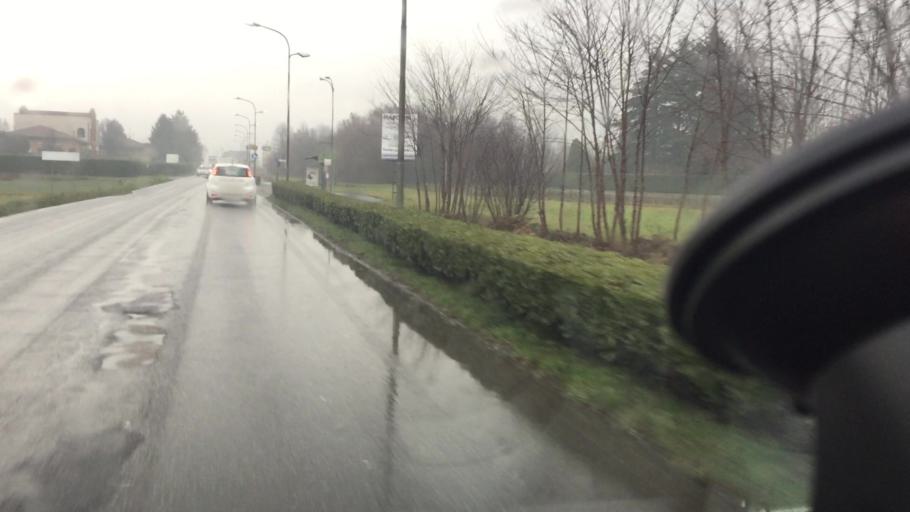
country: IT
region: Lombardy
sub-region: Citta metropolitana di Milano
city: Vaprio d'Adda
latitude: 45.5831
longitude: 9.5213
